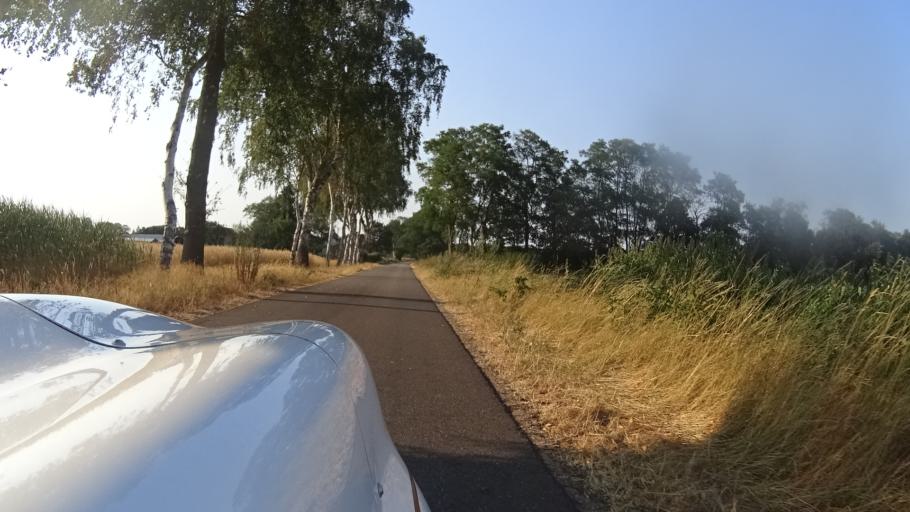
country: NL
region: North Brabant
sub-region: Gemeente Landerd
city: Zeeland
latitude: 51.7182
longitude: 5.6726
